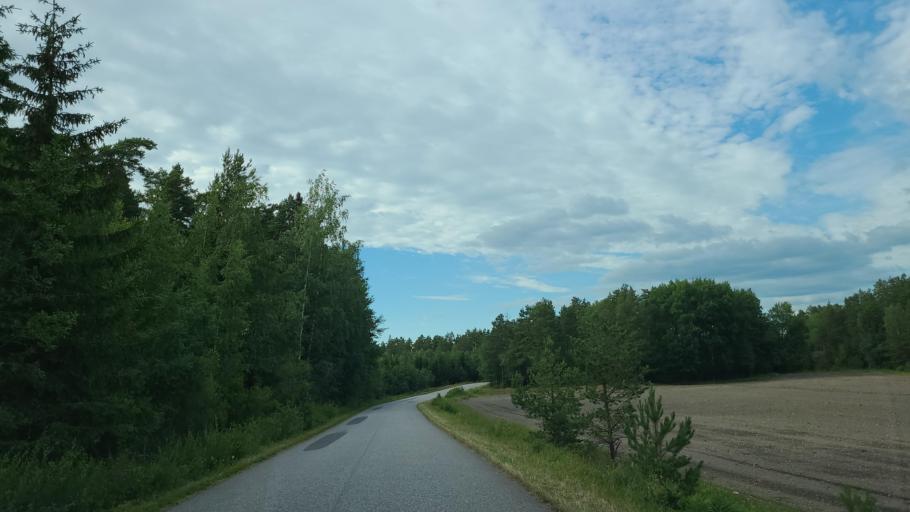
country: FI
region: Varsinais-Suomi
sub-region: Turku
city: Rymaettylae
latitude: 60.3056
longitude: 21.9409
